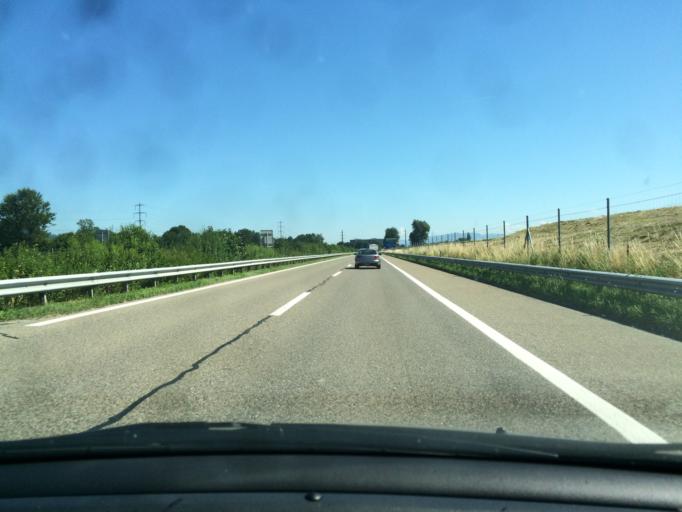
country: AT
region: Vorarlberg
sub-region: Politischer Bezirk Feldkirch
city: Mader
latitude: 47.3504
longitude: 9.6007
